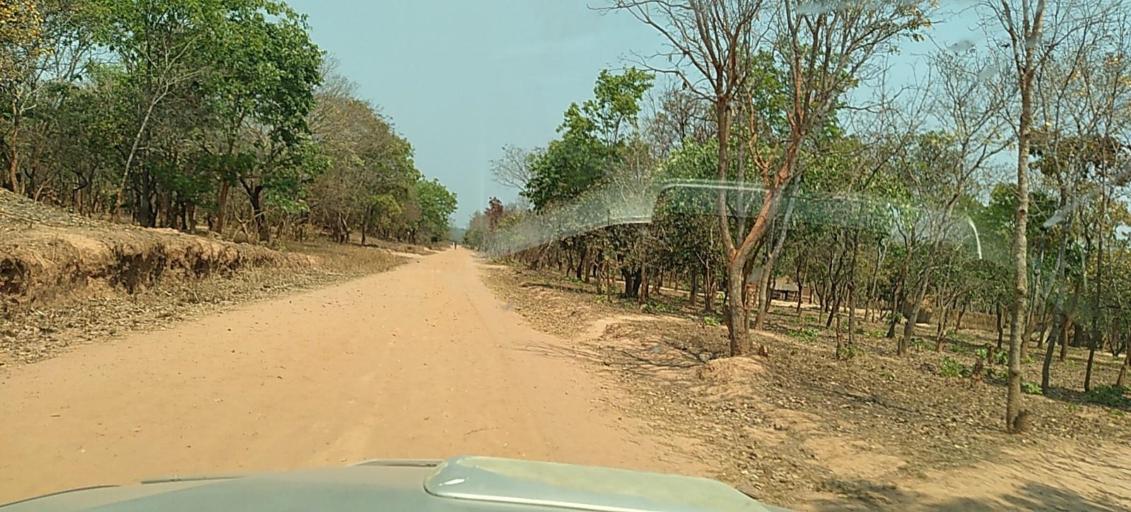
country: ZM
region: North-Western
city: Kasempa
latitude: -13.7035
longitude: 26.3330
